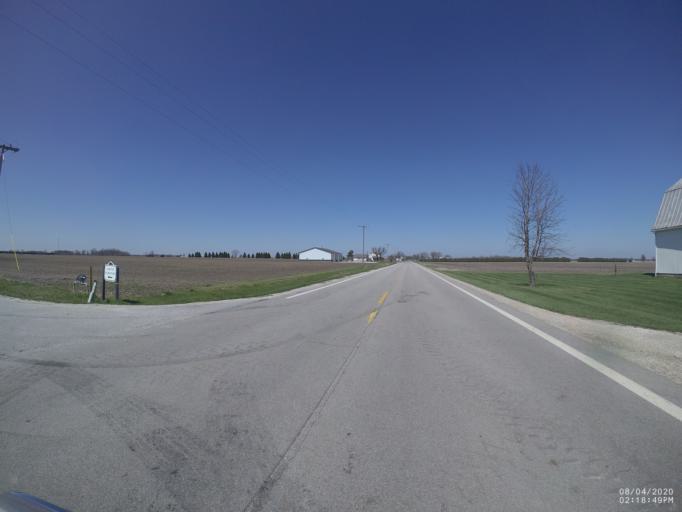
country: US
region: Ohio
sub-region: Sandusky County
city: Stony Prairie
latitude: 41.2894
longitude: -83.2356
